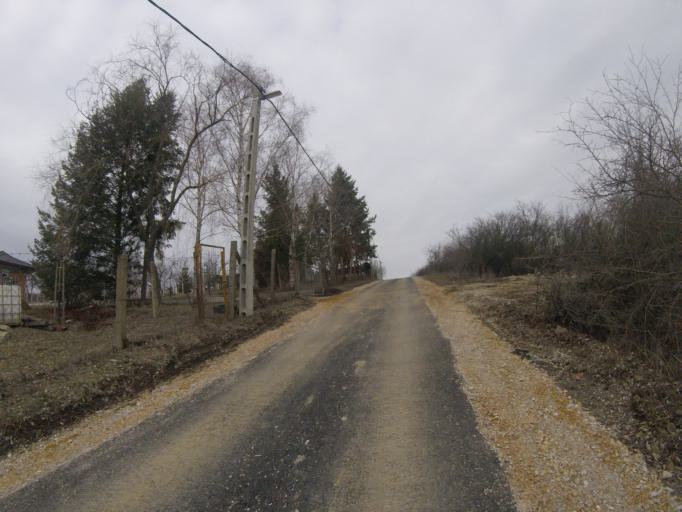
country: HU
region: Heves
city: Egerszalok
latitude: 47.8604
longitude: 20.3347
